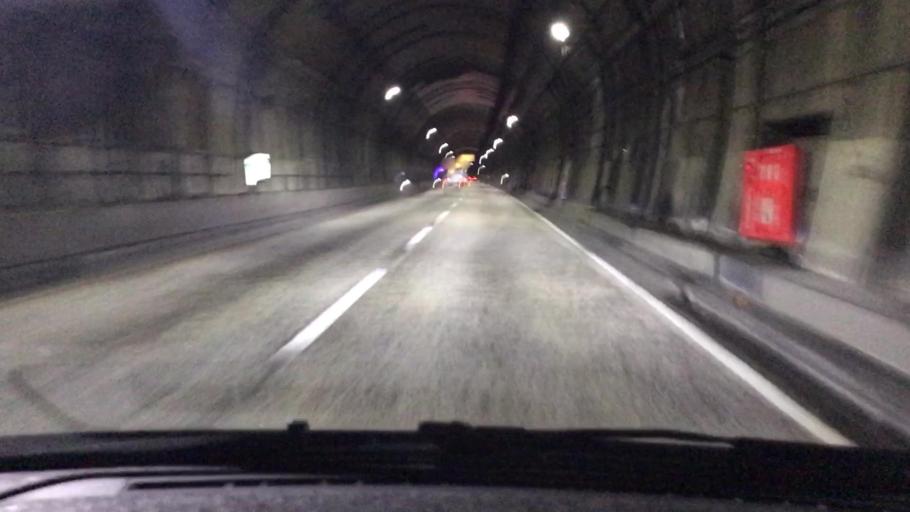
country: JP
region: Hyogo
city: Kobe
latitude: 34.7081
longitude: 135.1938
